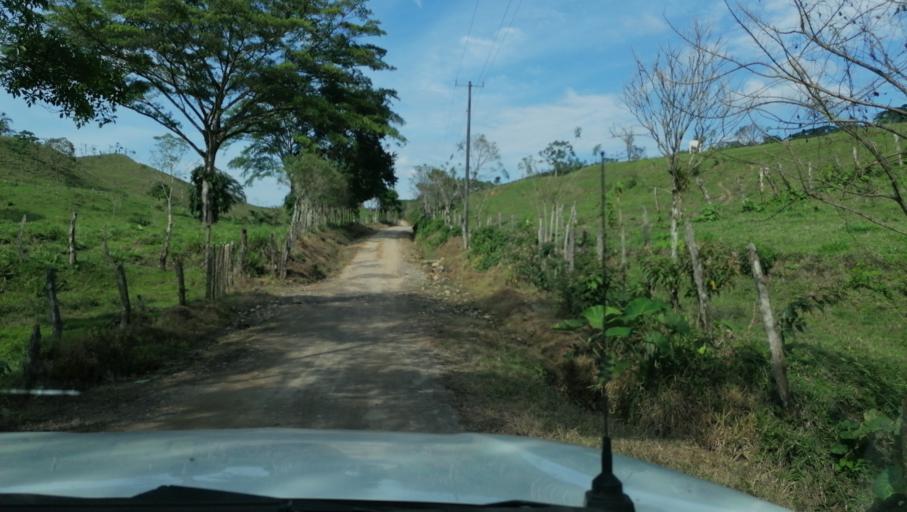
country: MX
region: Chiapas
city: Ostuacan
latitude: 17.4629
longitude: -93.2390
